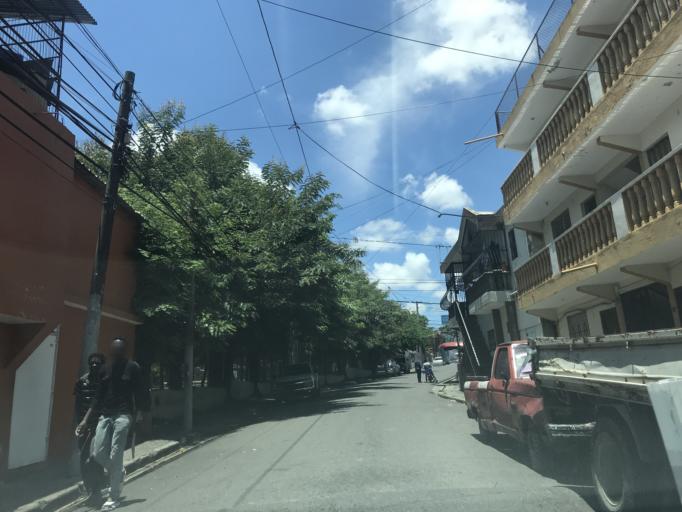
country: DO
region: Santiago
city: Santiago de los Caballeros
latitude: 19.4368
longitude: -70.6948
